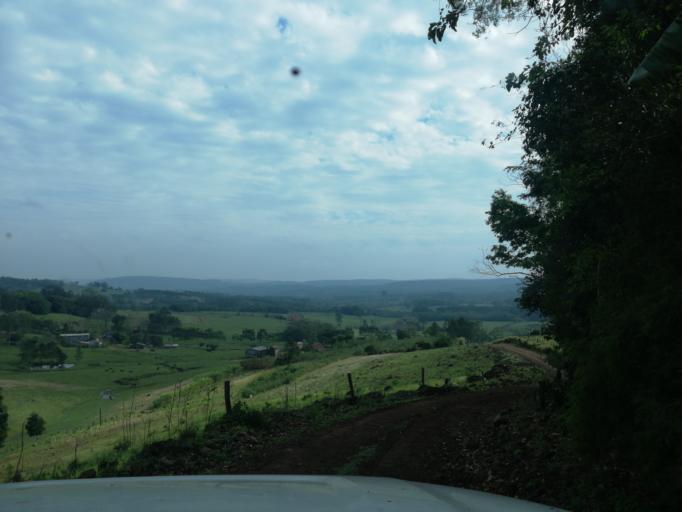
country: AR
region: Misiones
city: Cerro Azul
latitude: -27.6146
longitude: -55.5021
